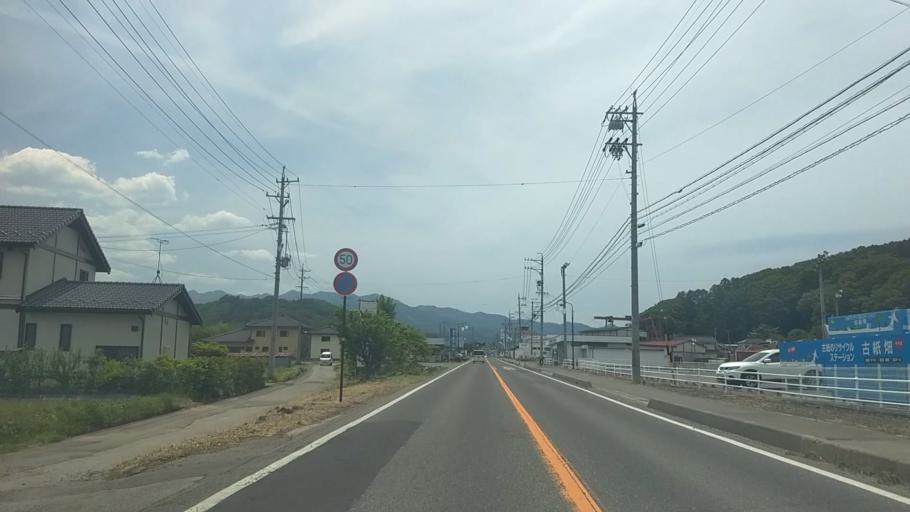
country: JP
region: Nagano
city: Saku
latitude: 36.1742
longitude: 138.4853
